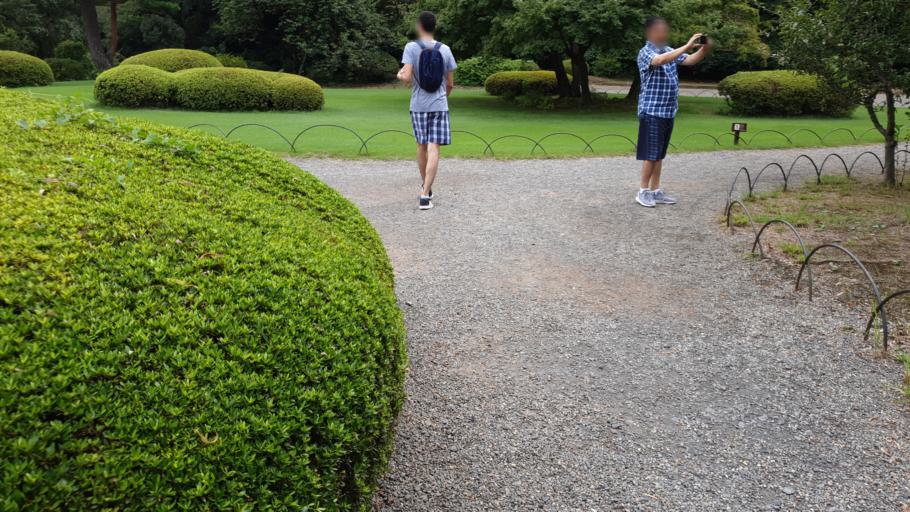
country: JP
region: Tokyo
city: Tokyo
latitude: 35.6854
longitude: 139.7059
